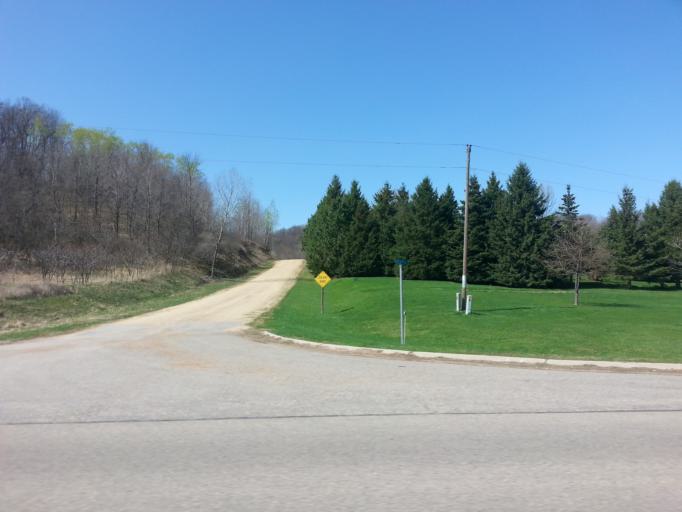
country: US
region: Wisconsin
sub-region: Dunn County
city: Menomonie
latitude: 44.8888
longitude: -92.0584
